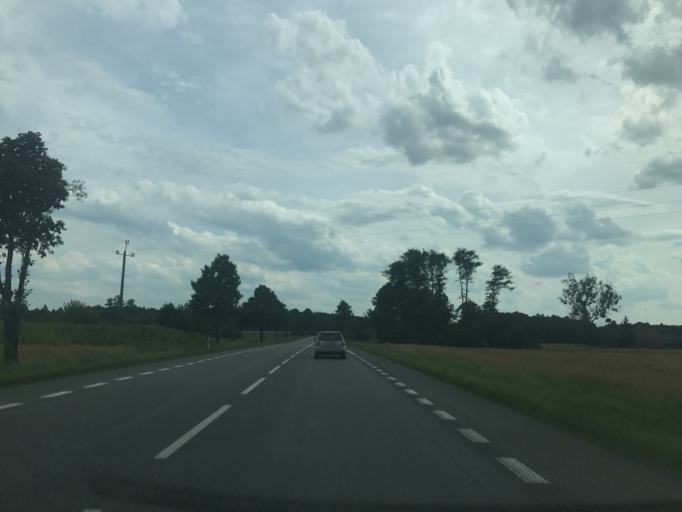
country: PL
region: Masovian Voivodeship
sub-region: Powiat mlawski
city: Strzegowo
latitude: 52.9325
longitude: 20.2849
